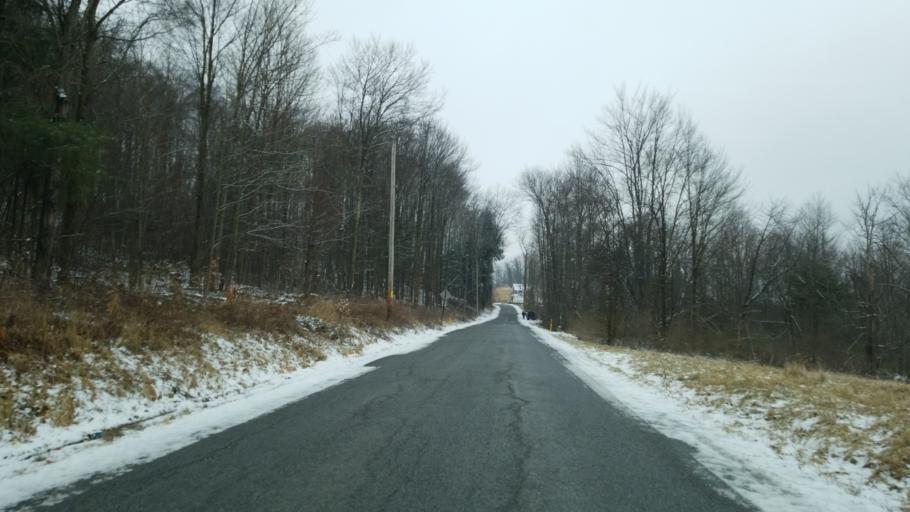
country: US
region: Pennsylvania
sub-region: Jefferson County
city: Sykesville
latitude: 41.0797
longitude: -78.7985
